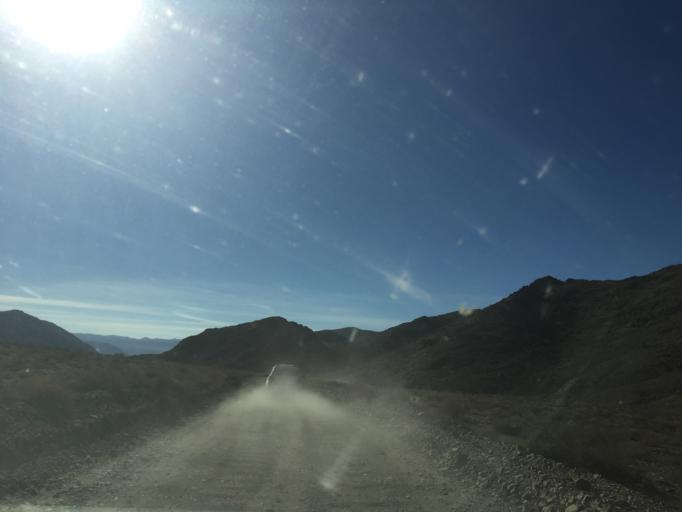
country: US
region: California
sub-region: Inyo County
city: Lone Pine
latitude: 36.8008
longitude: -117.5152
